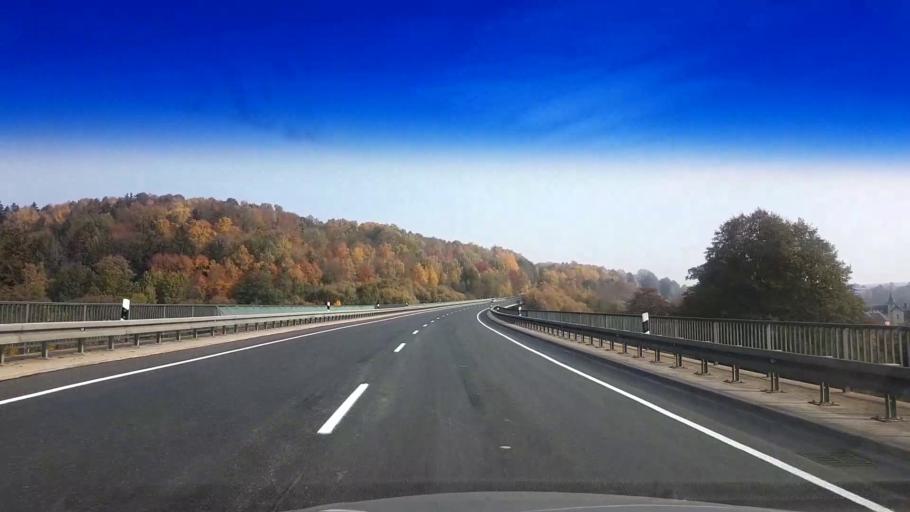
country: DE
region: Bavaria
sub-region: Upper Franconia
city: Arzberg
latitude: 50.0579
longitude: 12.1728
